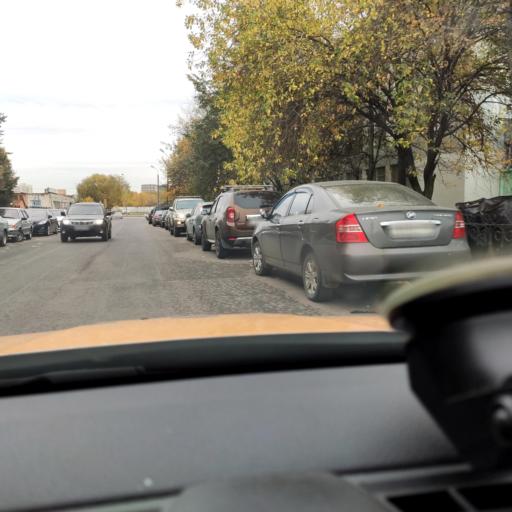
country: RU
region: Moskovskaya
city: Vostryakovo
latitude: 55.6685
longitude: 37.4364
